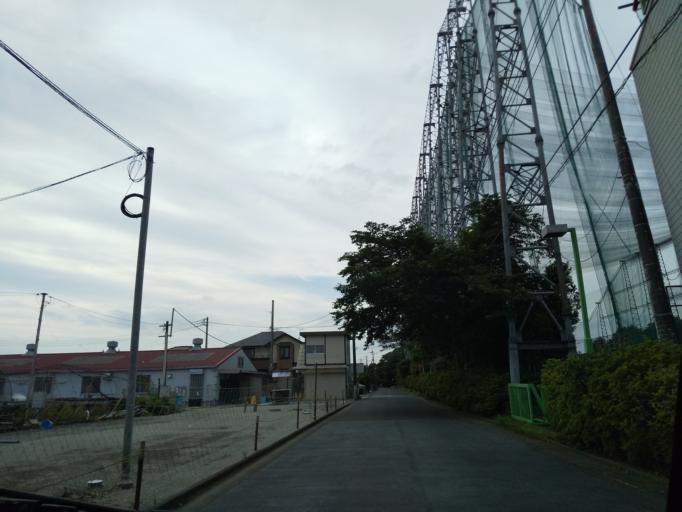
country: JP
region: Kanagawa
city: Zama
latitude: 35.4730
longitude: 139.3609
